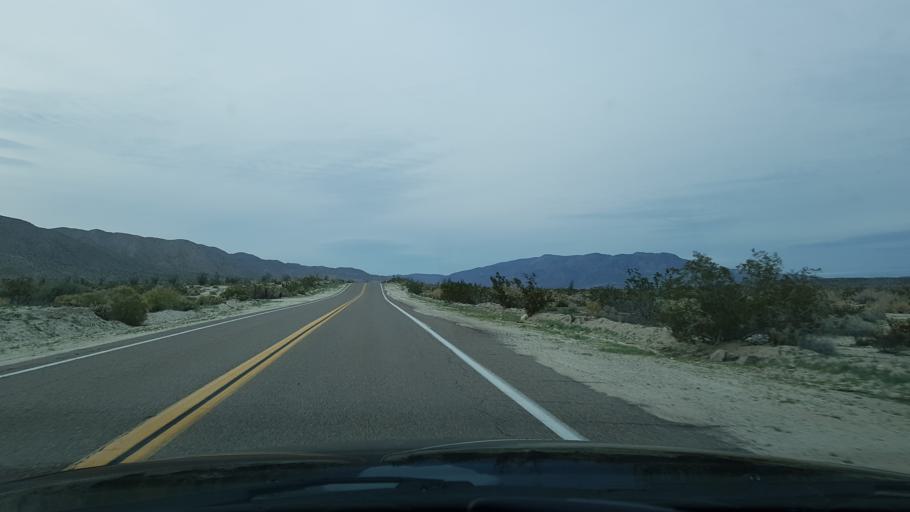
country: US
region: California
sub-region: San Diego County
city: Pine Valley
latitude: 32.8790
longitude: -116.2105
